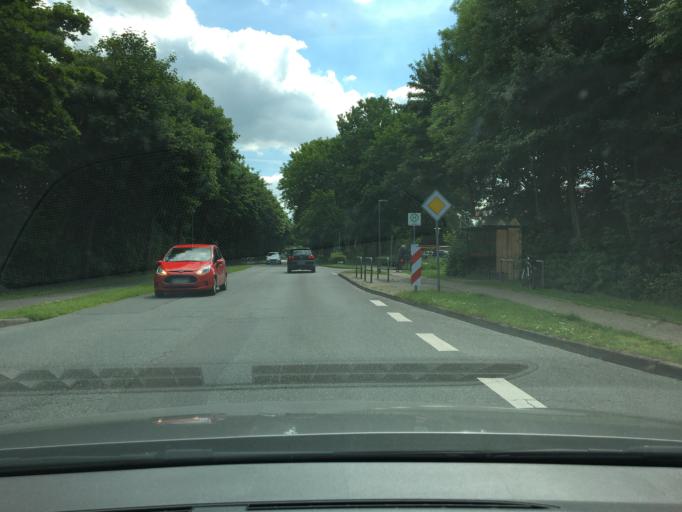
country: DE
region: Schleswig-Holstein
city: Kropp
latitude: 54.4148
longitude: 9.5014
